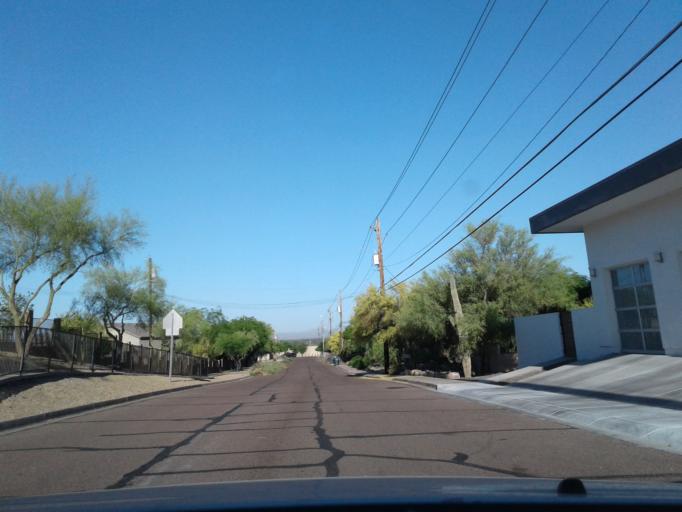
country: US
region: Arizona
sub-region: Maricopa County
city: Paradise Valley
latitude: 33.5421
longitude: -112.0367
